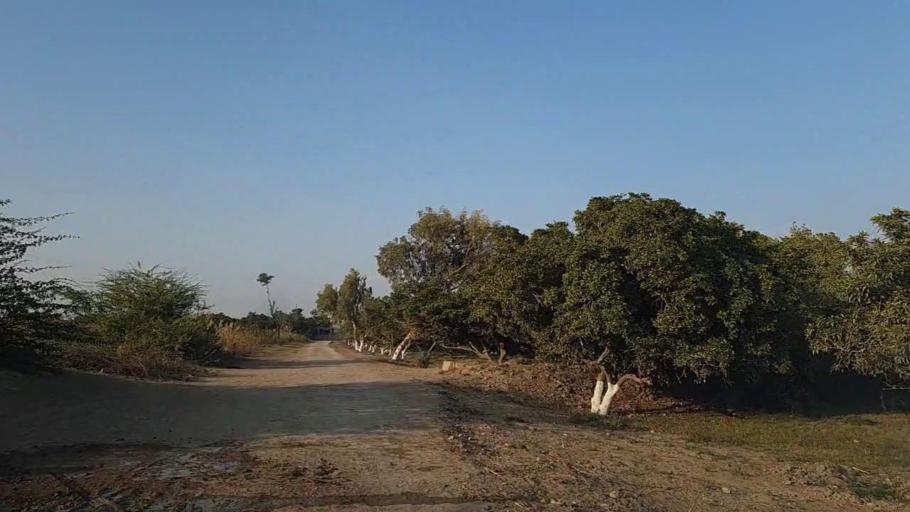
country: PK
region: Sindh
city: Naukot
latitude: 24.9295
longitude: 69.4380
